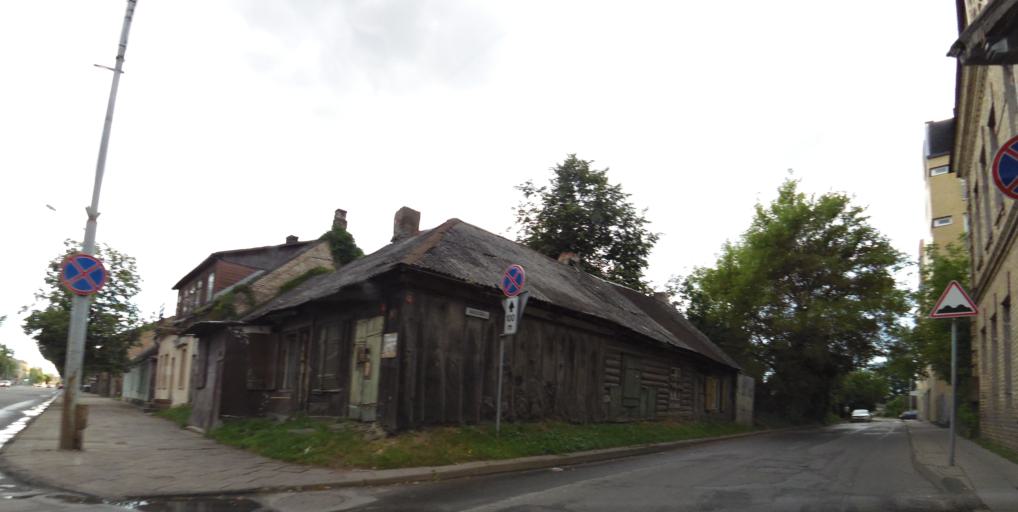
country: LT
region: Vilnius County
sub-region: Vilnius
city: Vilnius
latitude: 54.7025
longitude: 25.2834
